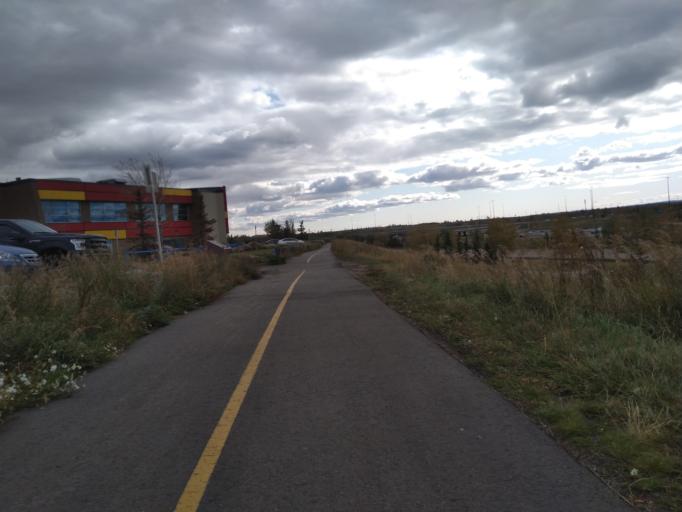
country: CA
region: Alberta
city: Calgary
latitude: 51.0428
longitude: -114.0057
